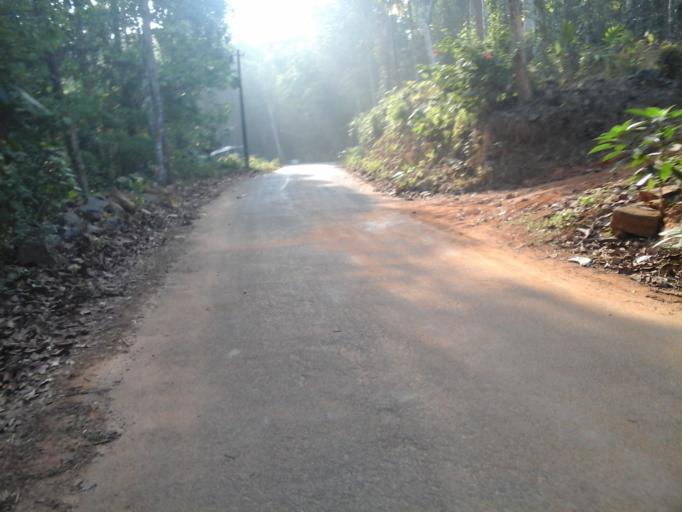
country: IN
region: Kerala
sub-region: Kottayam
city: Erattupetta
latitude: 9.5926
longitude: 76.7204
